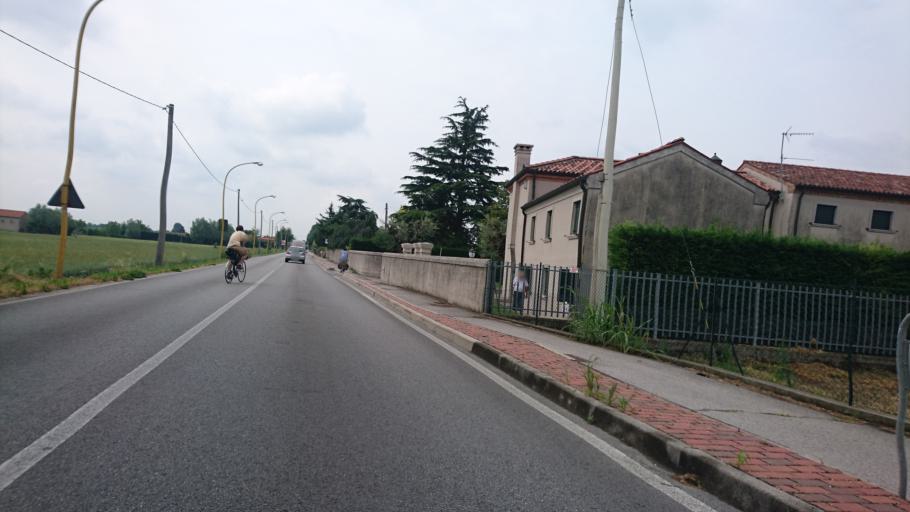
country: IT
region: Veneto
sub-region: Provincia di Padova
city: Villa Estense
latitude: 45.1821
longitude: 11.6714
